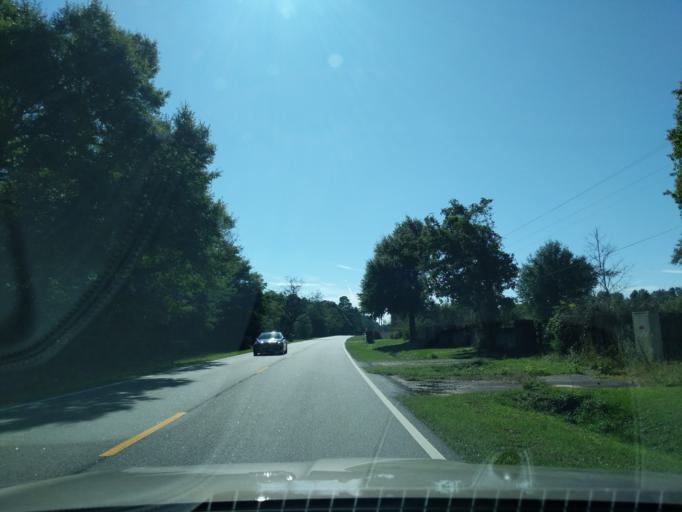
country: US
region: Georgia
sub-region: Richmond County
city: Hephzibah
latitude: 33.2678
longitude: -82.0101
